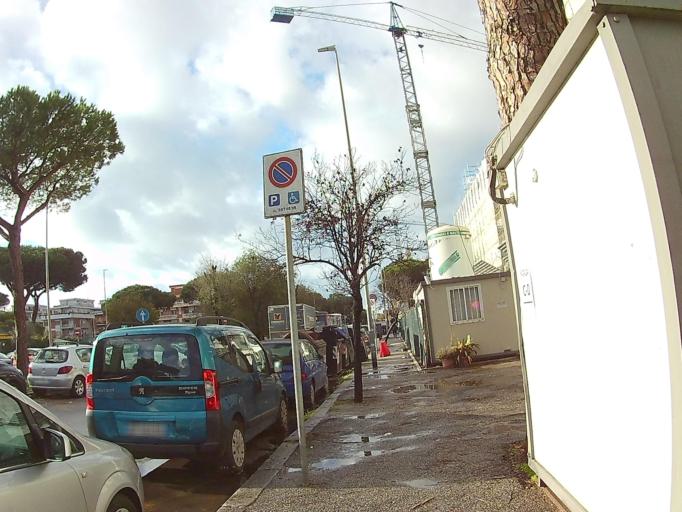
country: IT
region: Latium
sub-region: Citta metropolitana di Roma Capitale
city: Lido di Ostia
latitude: 41.7355
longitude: 12.2887
